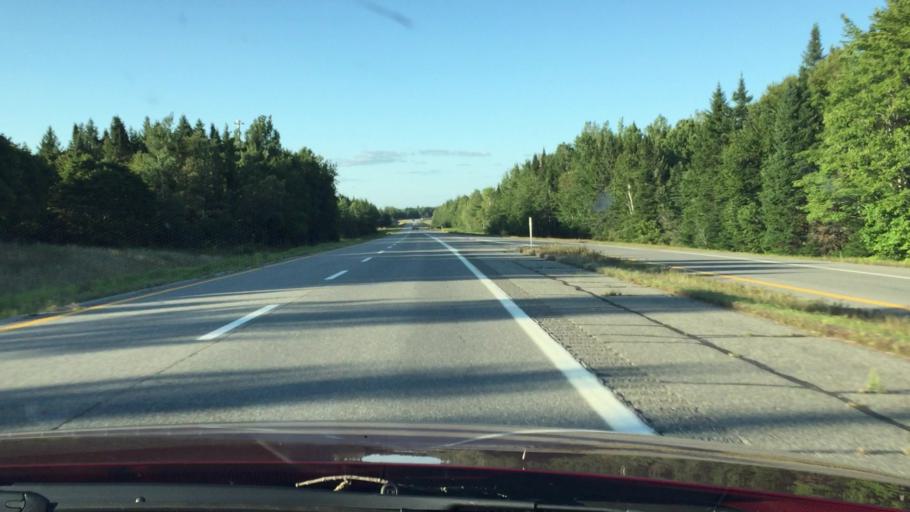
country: US
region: Maine
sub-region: Penobscot County
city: Patten
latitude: 45.8751
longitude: -68.4112
